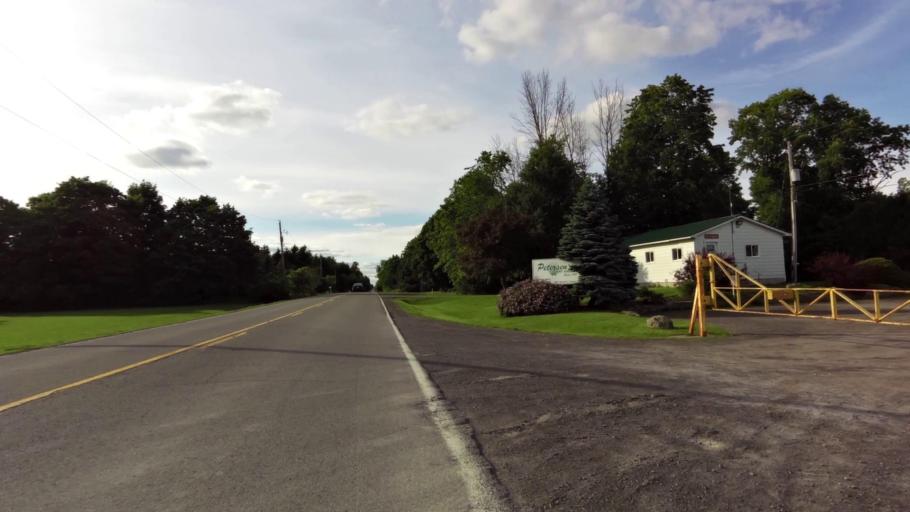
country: CA
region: Ontario
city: Ottawa
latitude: 45.1980
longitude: -75.5901
